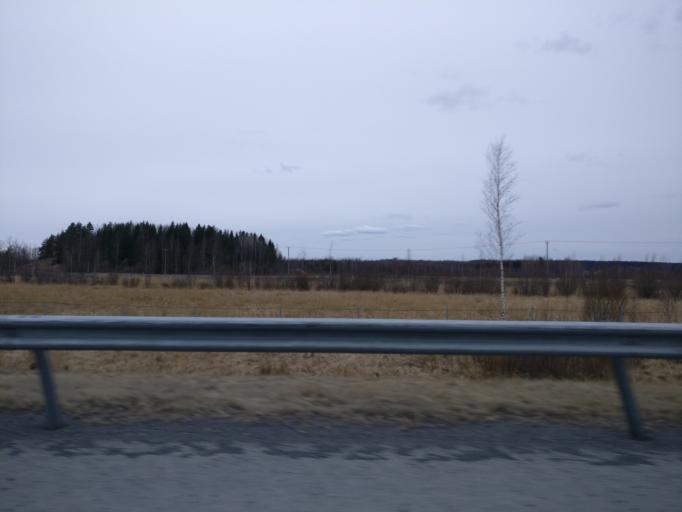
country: FI
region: Pirkanmaa
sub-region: Tampere
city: Lempaeaelae
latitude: 61.3412
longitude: 23.7902
